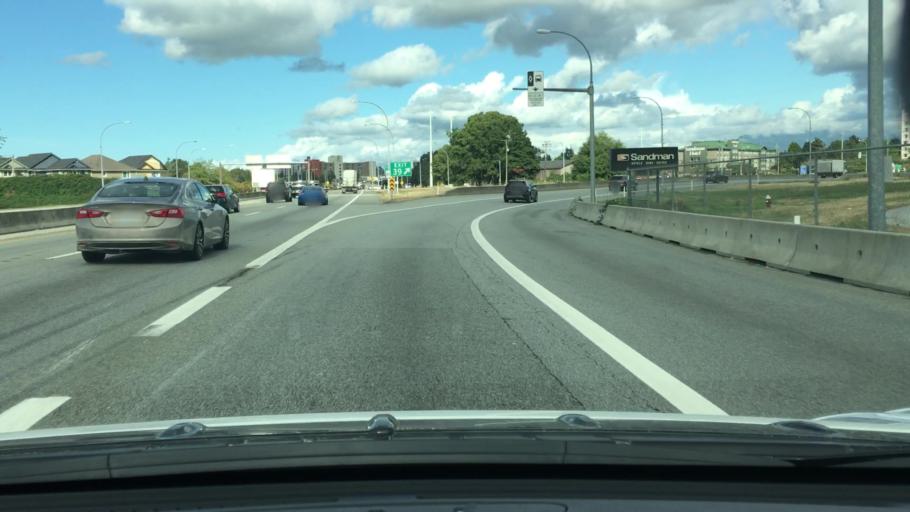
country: CA
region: British Columbia
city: Richmond
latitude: 49.1877
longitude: -123.1121
